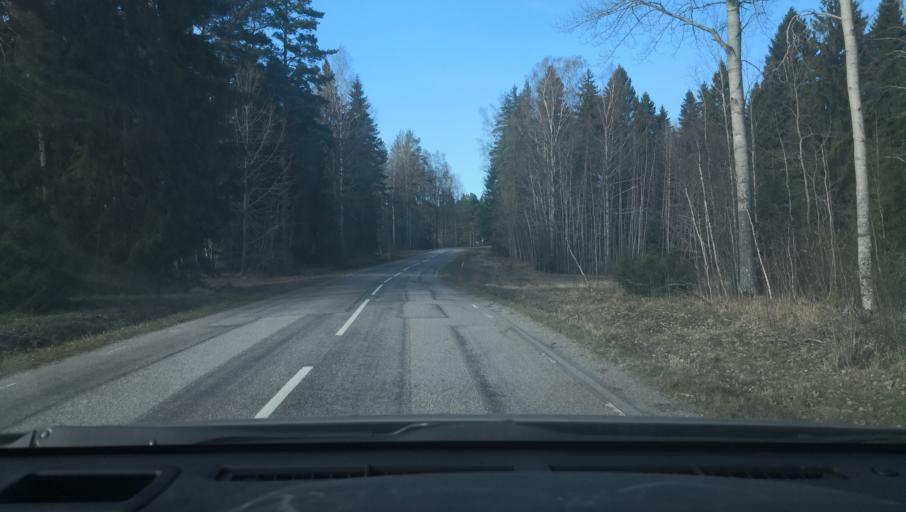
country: SE
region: Uppsala
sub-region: Heby Kommun
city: Heby
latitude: 59.9802
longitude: 16.9069
